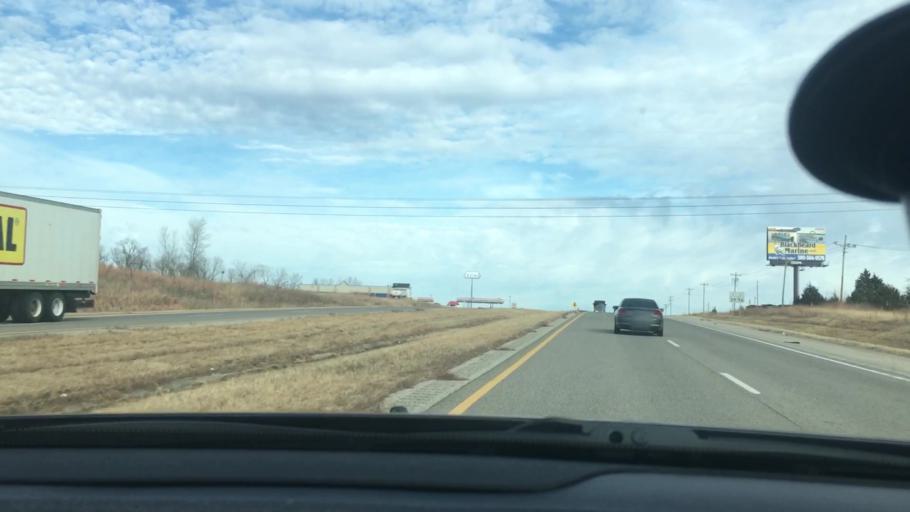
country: US
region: Oklahoma
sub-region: Seminole County
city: Konawa
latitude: 34.9366
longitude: -96.6832
